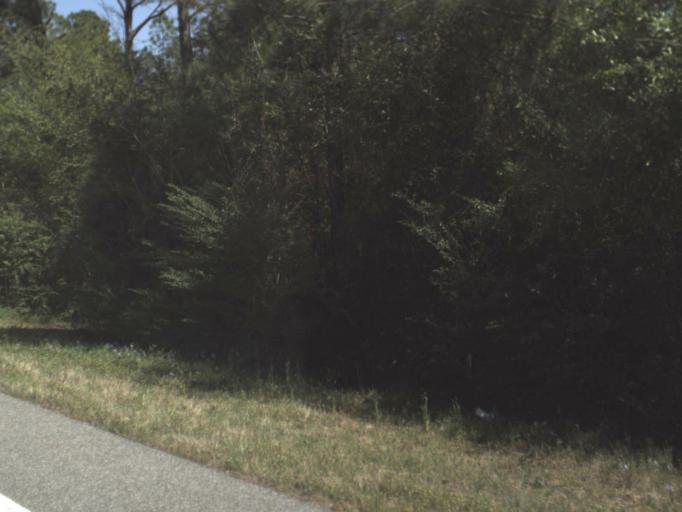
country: US
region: Florida
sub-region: Okaloosa County
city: Crestview
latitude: 30.7223
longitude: -86.7304
